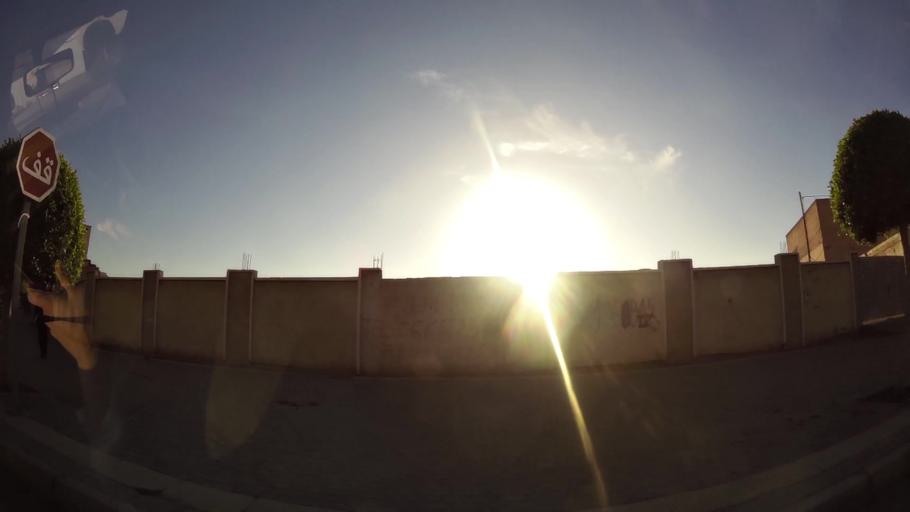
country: MA
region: Oriental
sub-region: Oujda-Angad
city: Oujda
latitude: 34.6945
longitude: -1.9053
